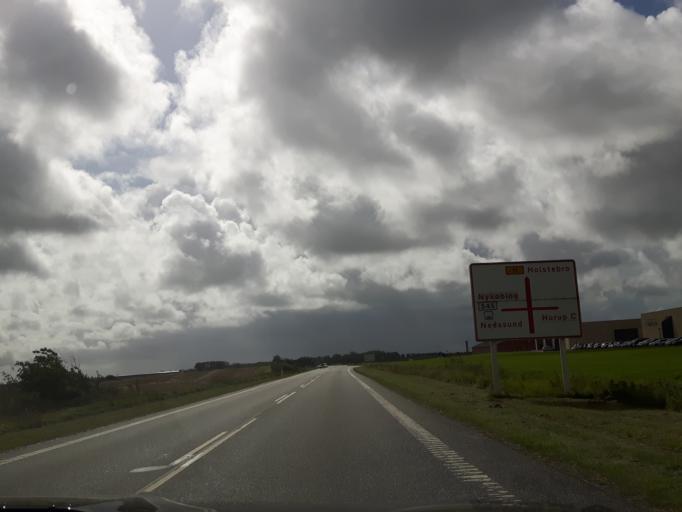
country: DK
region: North Denmark
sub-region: Thisted Kommune
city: Hurup
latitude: 56.7459
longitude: 8.4410
